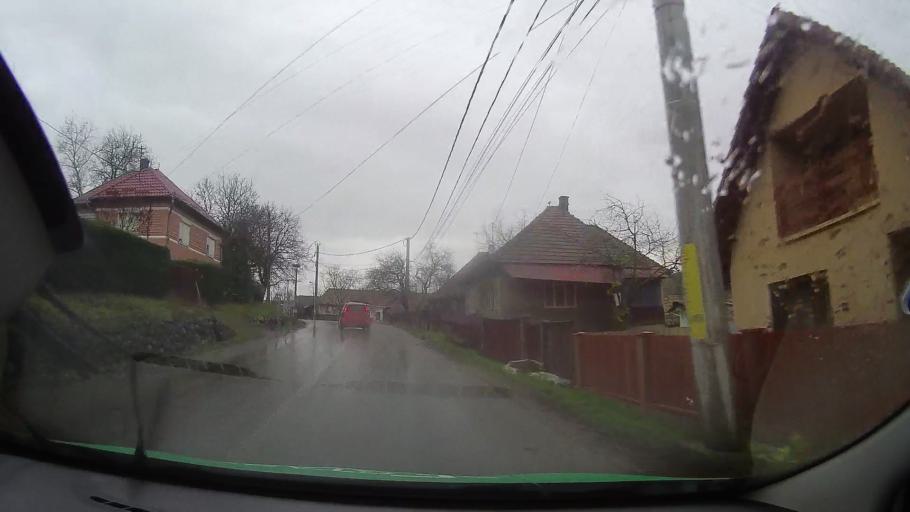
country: RO
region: Mures
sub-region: Comuna Vatava
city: Vatava
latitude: 46.9357
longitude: 24.7681
